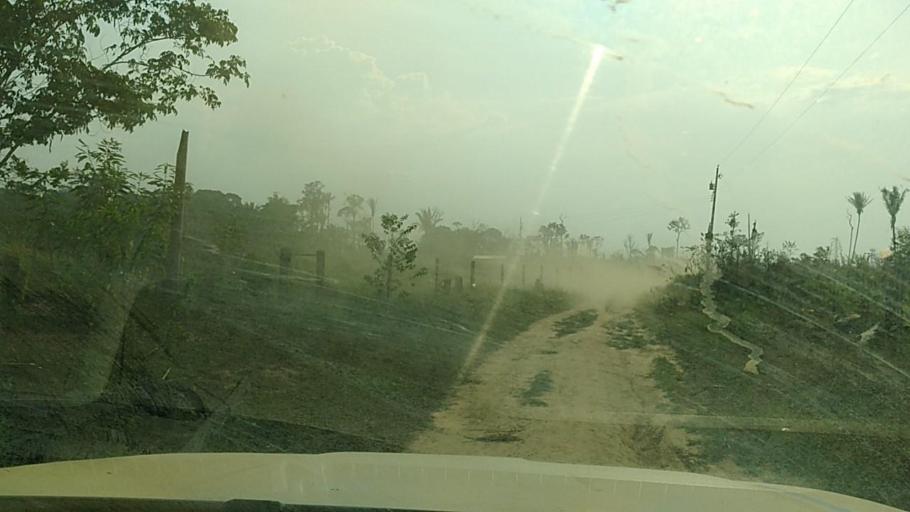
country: BR
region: Rondonia
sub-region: Porto Velho
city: Porto Velho
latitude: -8.5641
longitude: -64.0361
